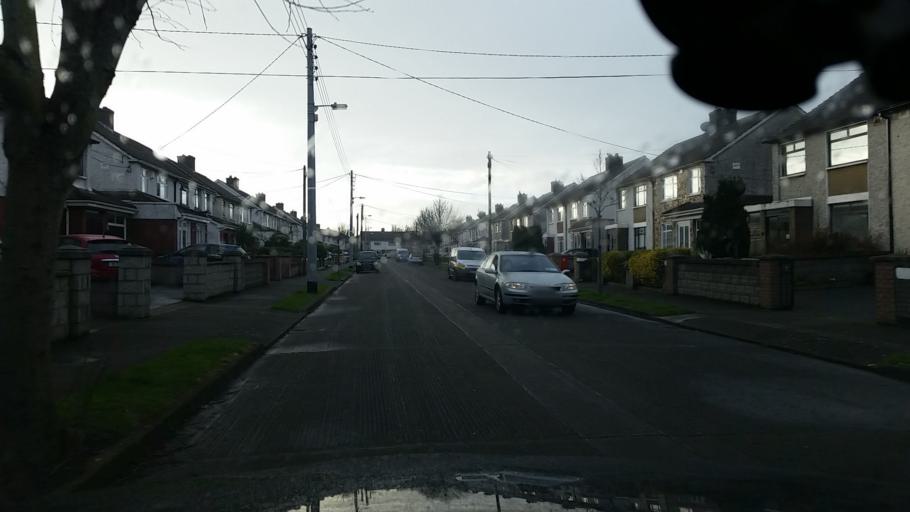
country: IE
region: Leinster
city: Artane
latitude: 53.3896
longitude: -6.2104
